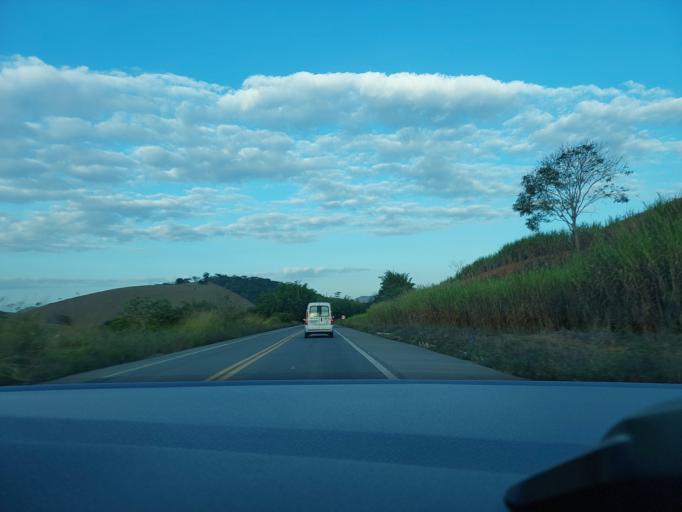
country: BR
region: Minas Gerais
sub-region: Muriae
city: Muriae
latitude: -21.1377
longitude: -42.1778
